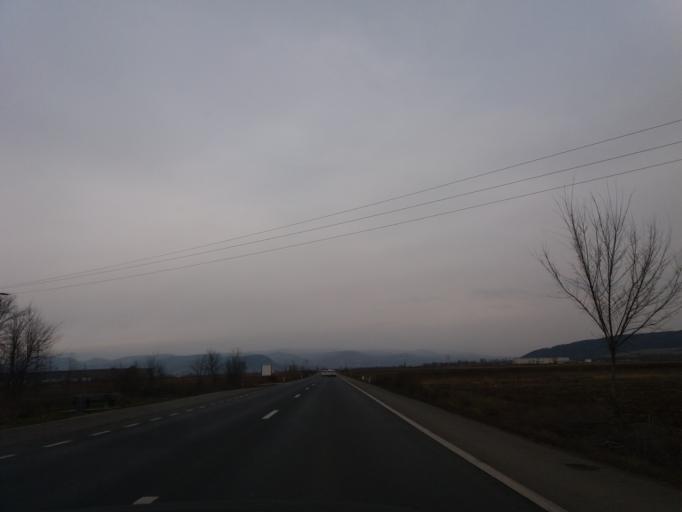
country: RO
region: Hunedoara
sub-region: Comuna Bacia
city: Bacia
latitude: 45.8083
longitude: 23.0152
